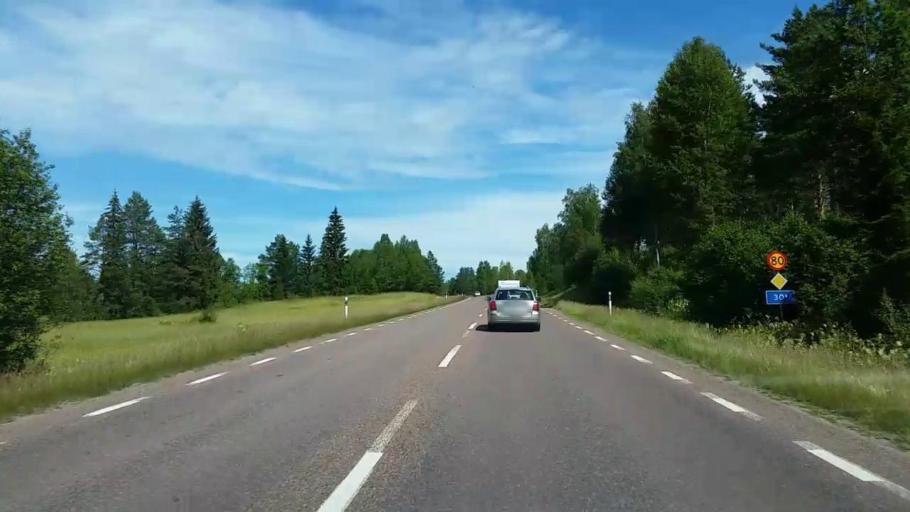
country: SE
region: Dalarna
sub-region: Rattviks Kommun
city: Raettvik
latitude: 60.9254
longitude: 15.2173
